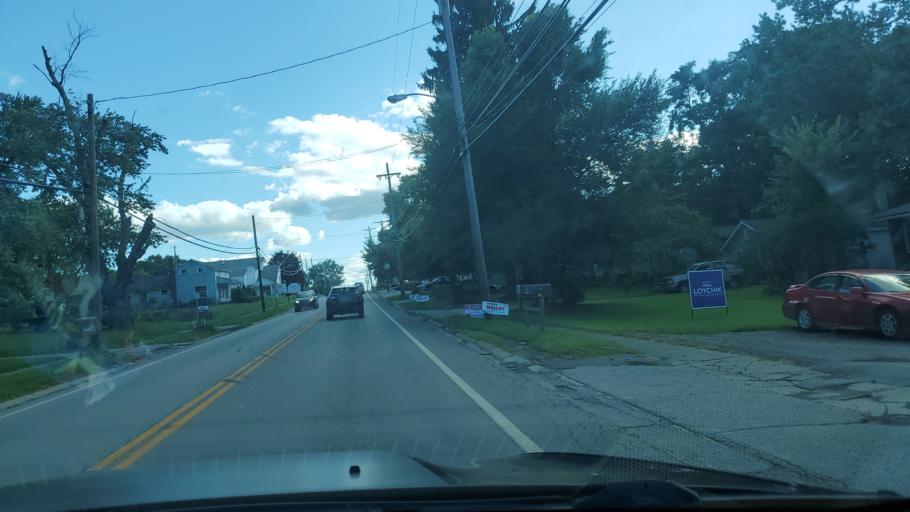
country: US
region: Ohio
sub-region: Trumbull County
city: Mineral Ridge
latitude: 41.1491
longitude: -80.7688
